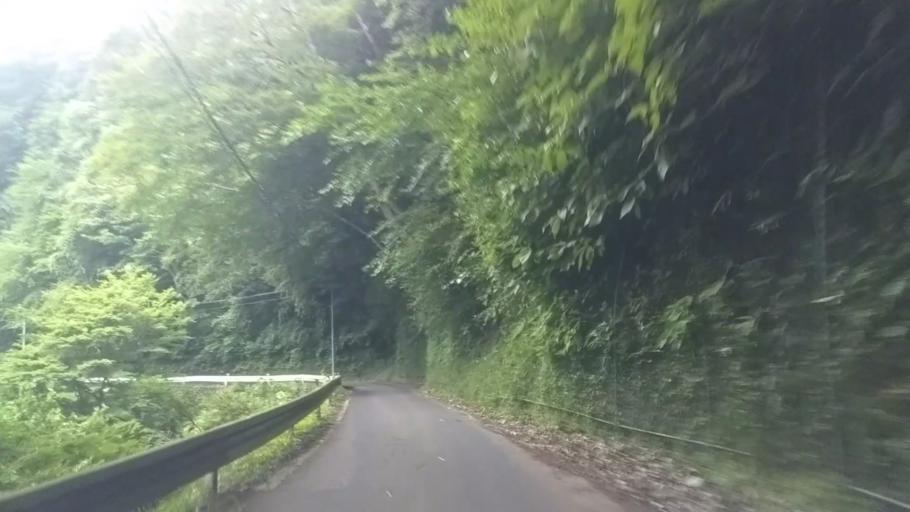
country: JP
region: Chiba
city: Kawaguchi
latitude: 35.2048
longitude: 140.1405
